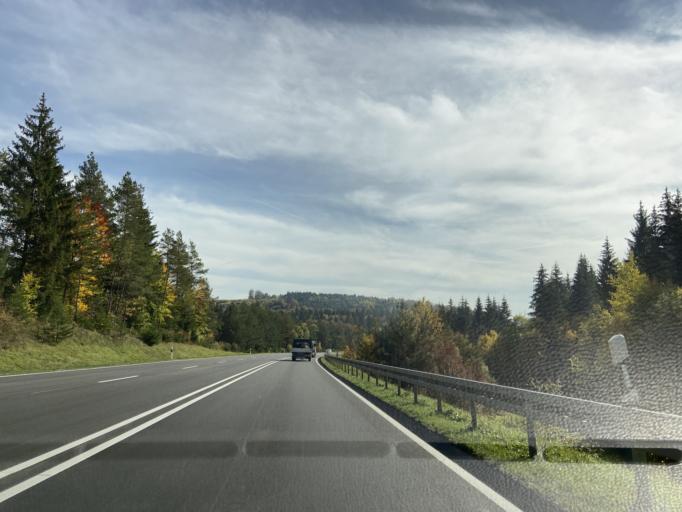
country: DE
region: Baden-Wuerttemberg
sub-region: Tuebingen Region
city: Sigmaringen
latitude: 48.1121
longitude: 9.2039
